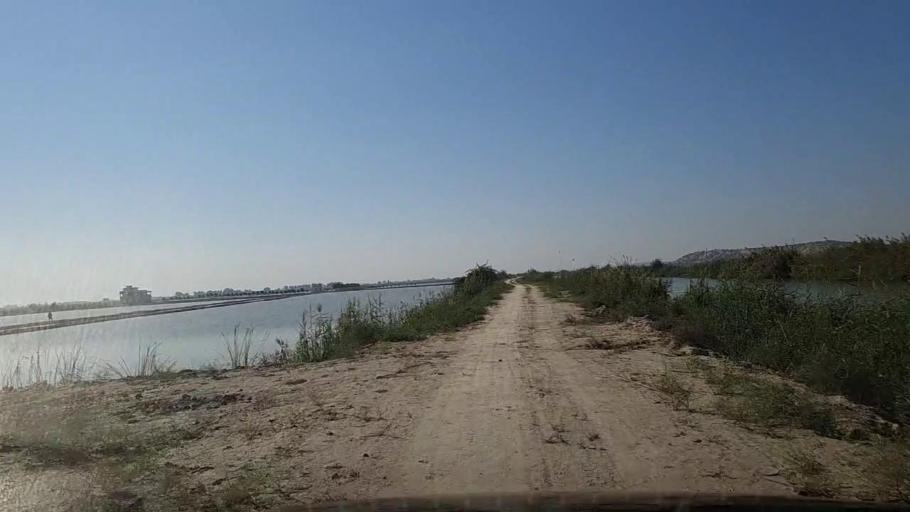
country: PK
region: Sindh
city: Thatta
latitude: 24.6844
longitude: 67.8919
